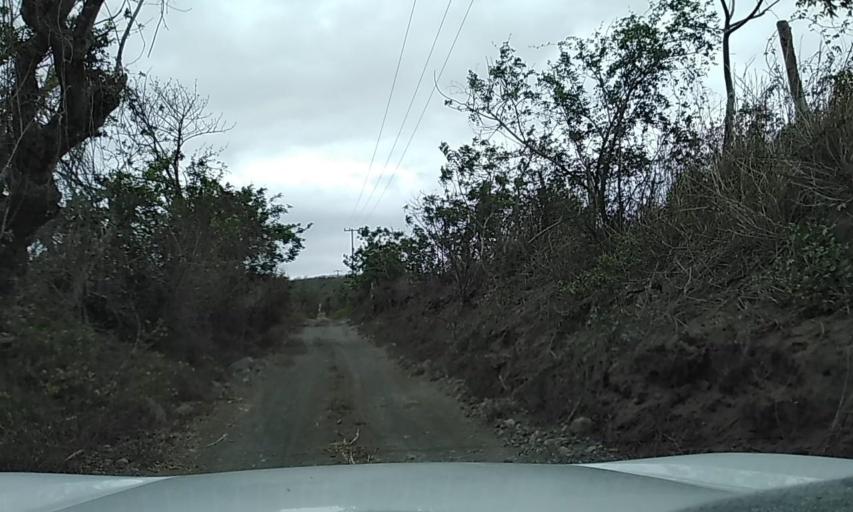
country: MX
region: Veracruz
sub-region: Veracruz
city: Delfino Victoria (Santa Fe)
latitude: 19.2753
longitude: -96.3142
